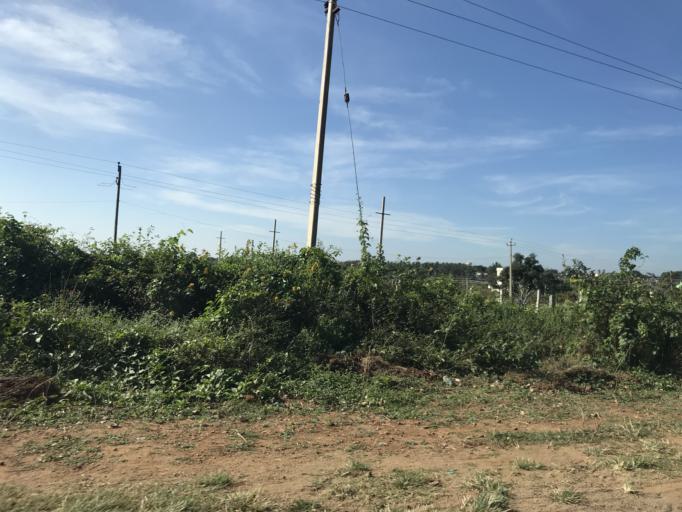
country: IN
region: Karnataka
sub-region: Mysore
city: Mysore
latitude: 12.2284
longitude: 76.5876
